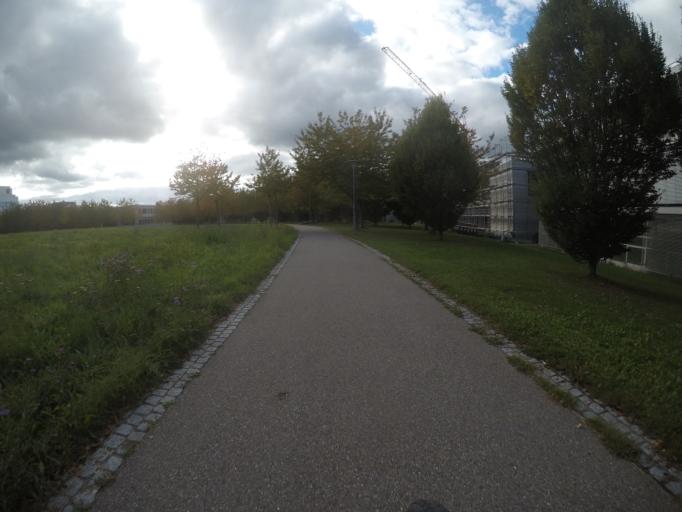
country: DE
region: Baden-Wuerttemberg
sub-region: Regierungsbezirk Stuttgart
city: Gerlingen
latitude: 48.7432
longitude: 9.0989
